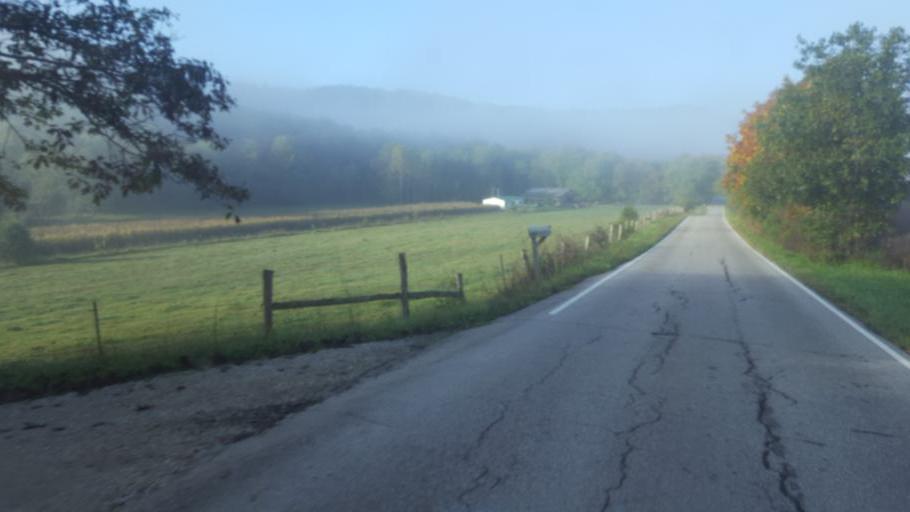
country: US
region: Ohio
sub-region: Adams County
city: Manchester
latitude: 38.5109
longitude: -83.5251
